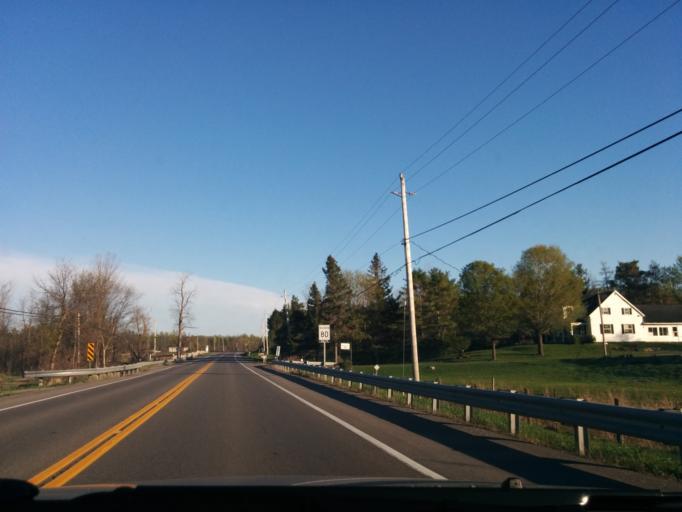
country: CA
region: Ontario
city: Ottawa
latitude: 45.1893
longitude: -75.6308
